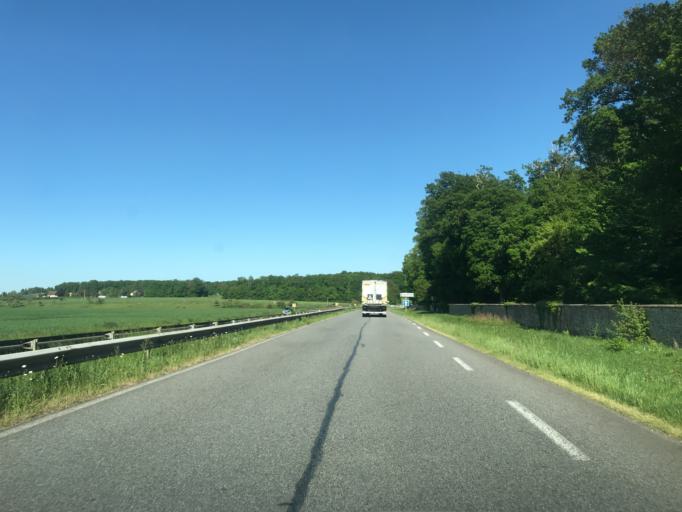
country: FR
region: Haute-Normandie
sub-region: Departement de l'Eure
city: Tillieres-sur-Avre
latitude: 48.7737
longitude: 1.1007
